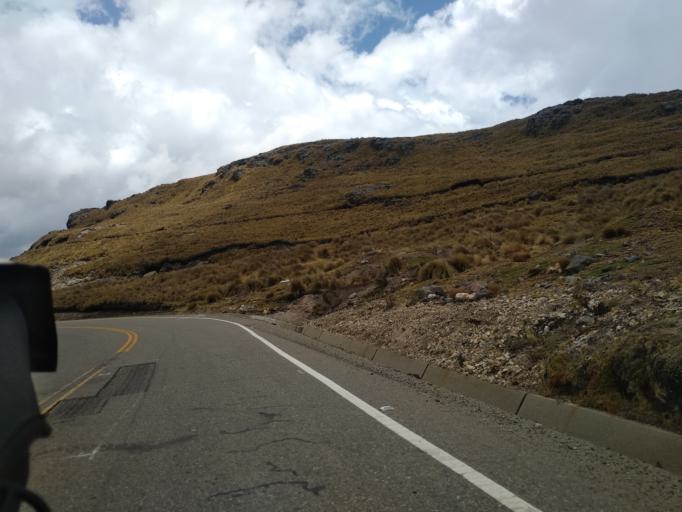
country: PE
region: La Libertad
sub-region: Provincia de Santiago de Chuco
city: Quiruvilca
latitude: -7.9729
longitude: -78.2075
